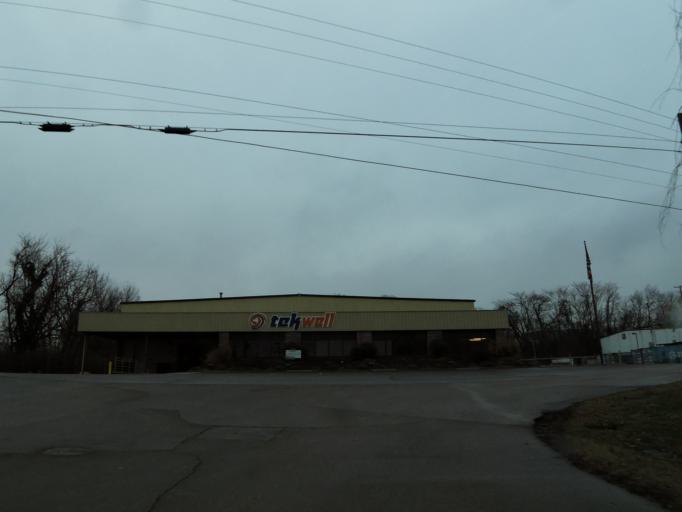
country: US
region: Tennessee
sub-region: Knox County
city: Knoxville
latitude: 35.9917
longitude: -83.9046
